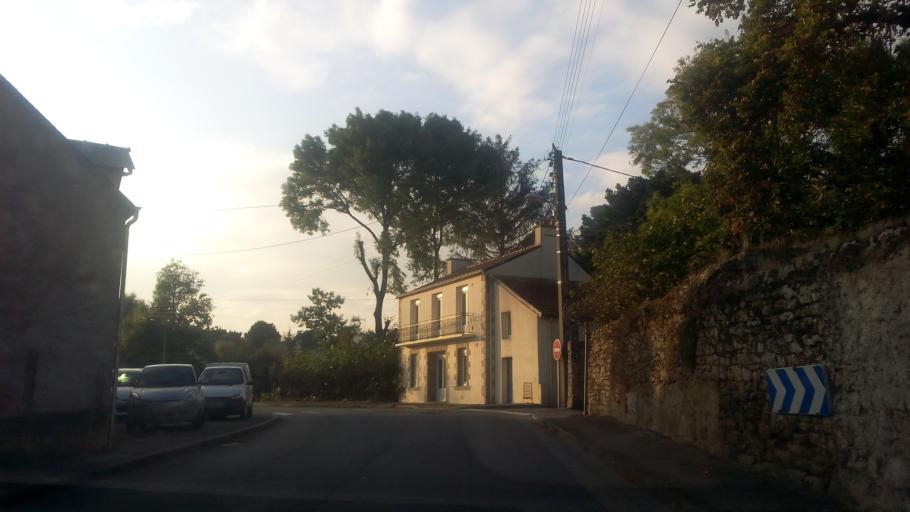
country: FR
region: Brittany
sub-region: Departement du Morbihan
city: Saint-Jean-la-Poterie
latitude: 47.6363
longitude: -2.1283
